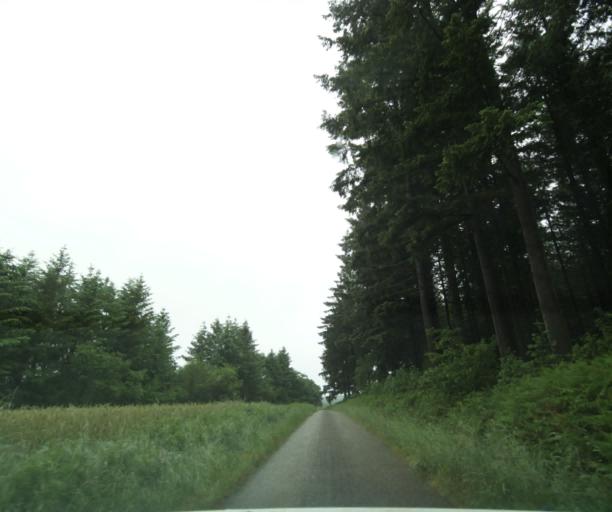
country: FR
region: Bourgogne
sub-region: Departement de Saone-et-Loire
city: Charolles
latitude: 46.4448
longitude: 4.3964
